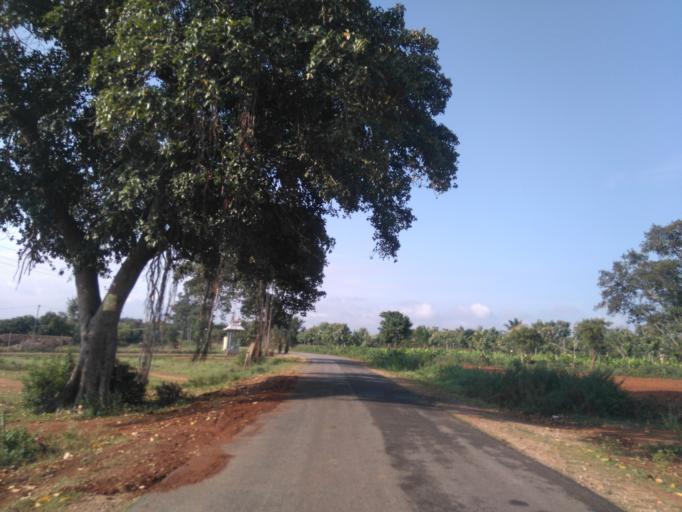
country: IN
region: Karnataka
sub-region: Mandya
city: Malavalli
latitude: 12.3062
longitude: 77.0724
